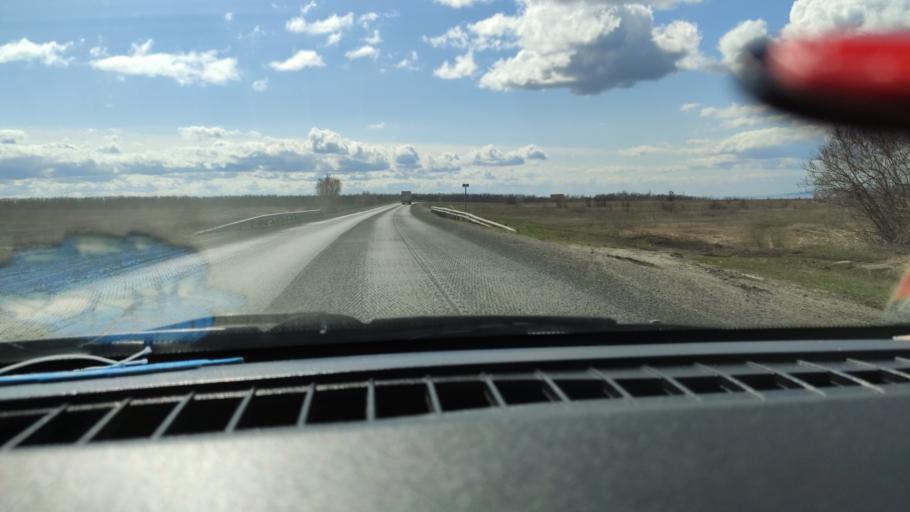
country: RU
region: Saratov
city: Dukhovnitskoye
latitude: 52.7123
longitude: 48.2665
